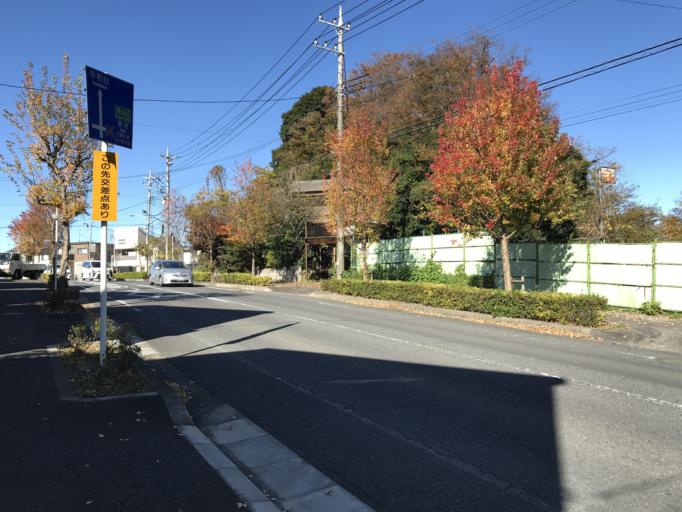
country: JP
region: Chiba
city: Nagareyama
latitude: 35.8463
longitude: 139.9110
